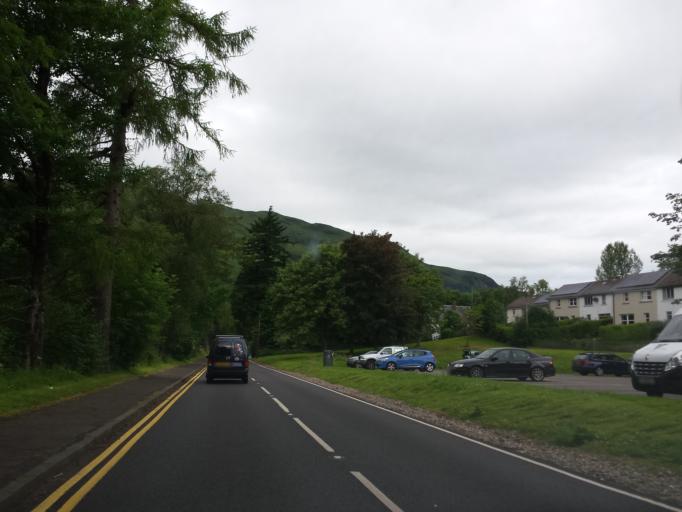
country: GB
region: Scotland
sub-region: Stirling
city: Callander
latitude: 56.3853
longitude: -4.2802
